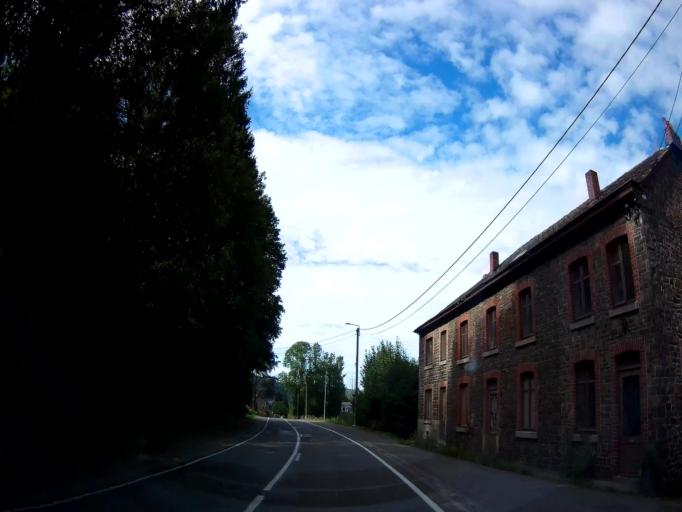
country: BE
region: Wallonia
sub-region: Province du Luxembourg
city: Rendeux
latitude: 50.2293
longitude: 5.5205
